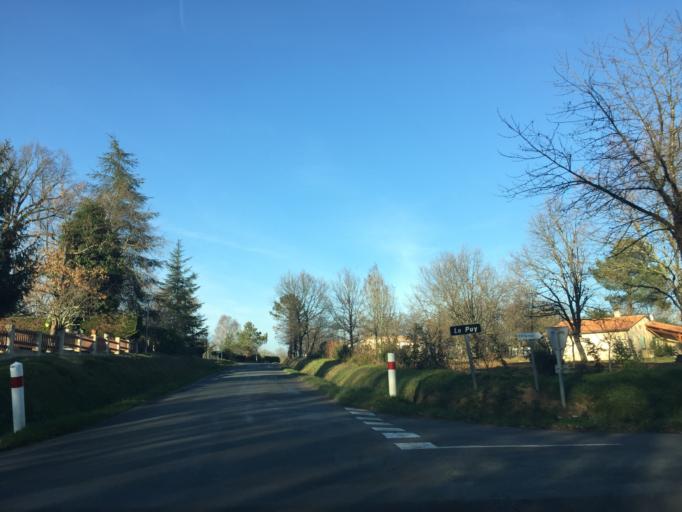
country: FR
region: Aquitaine
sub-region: Departement de la Dordogne
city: Riberac
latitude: 45.2172
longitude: 0.2942
